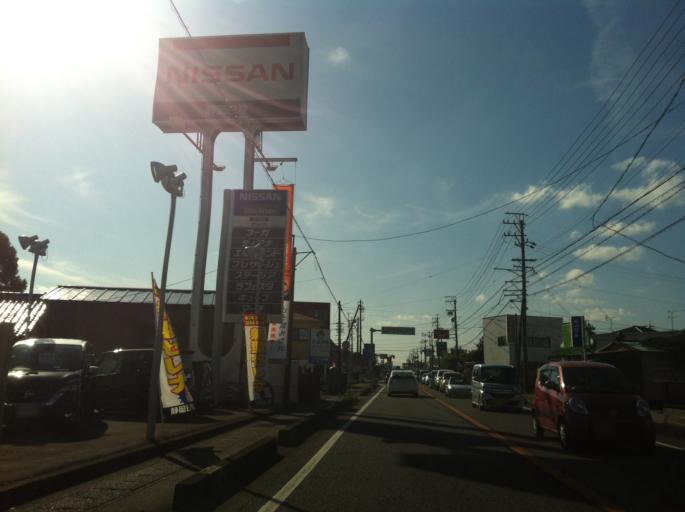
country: JP
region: Shizuoka
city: Fujieda
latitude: 34.8705
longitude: 138.2645
